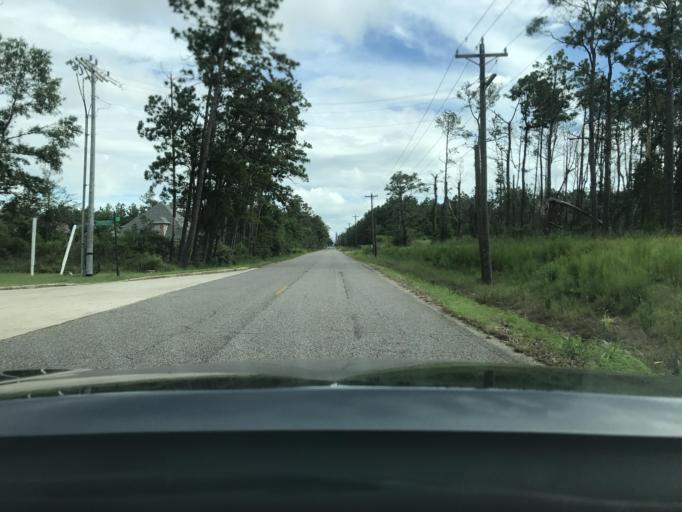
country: US
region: Louisiana
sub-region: Calcasieu Parish
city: Westlake
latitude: 30.2695
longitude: -93.2751
